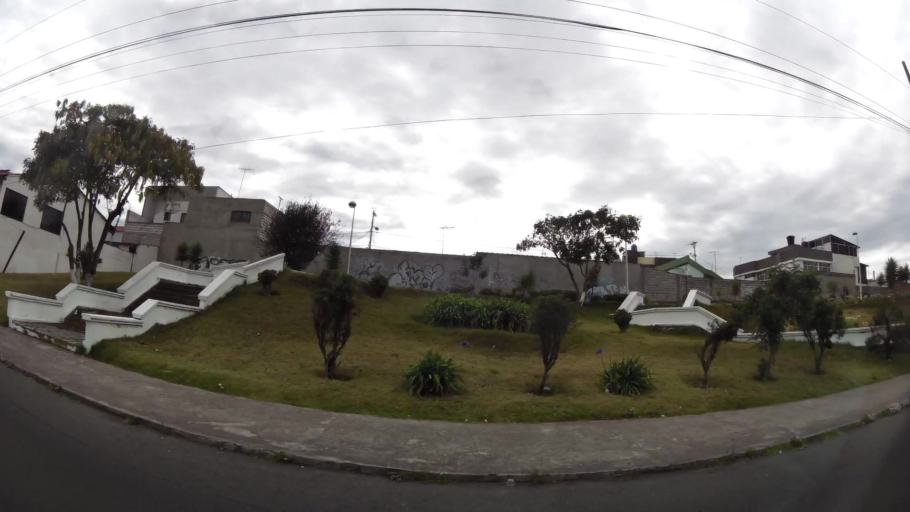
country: EC
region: Cotopaxi
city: Latacunga
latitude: -0.9411
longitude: -78.6166
